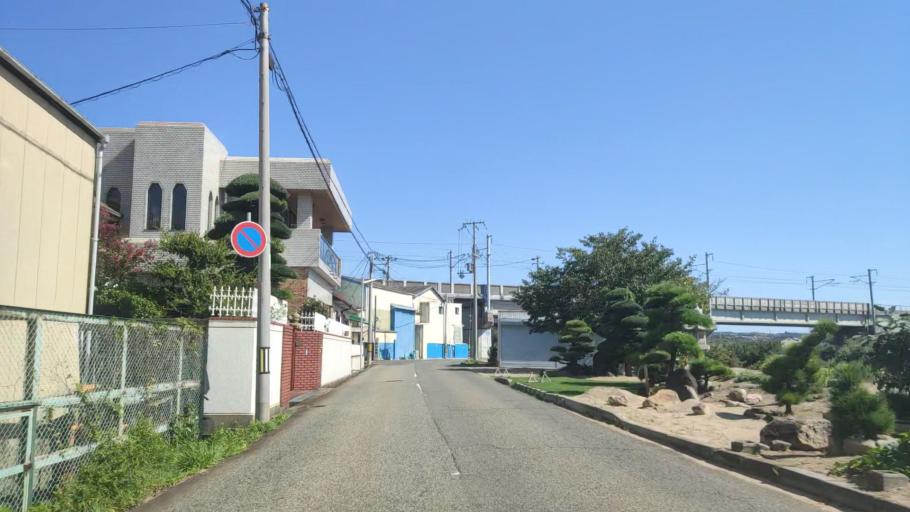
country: JP
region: Hyogo
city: Akashi
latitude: 34.6644
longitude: 134.9845
